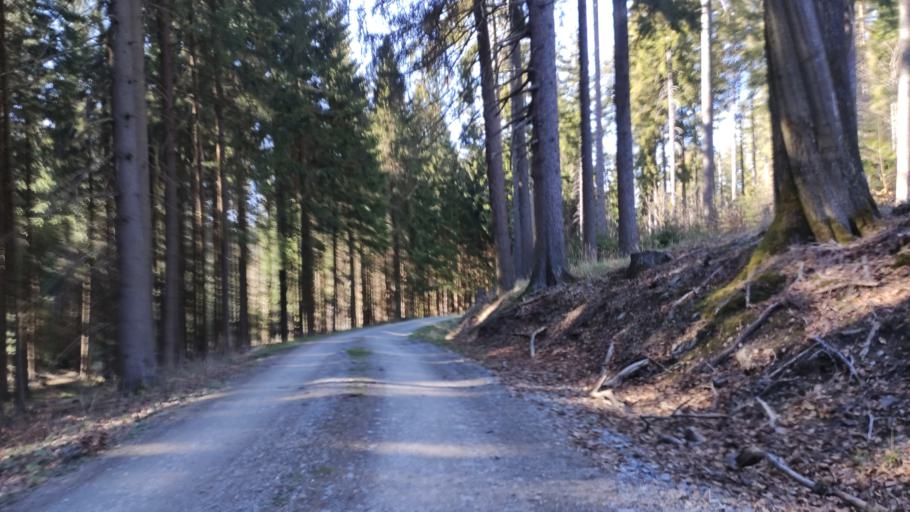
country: DE
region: Bavaria
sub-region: Upper Franconia
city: Reichenbach
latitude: 50.4505
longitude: 11.4374
